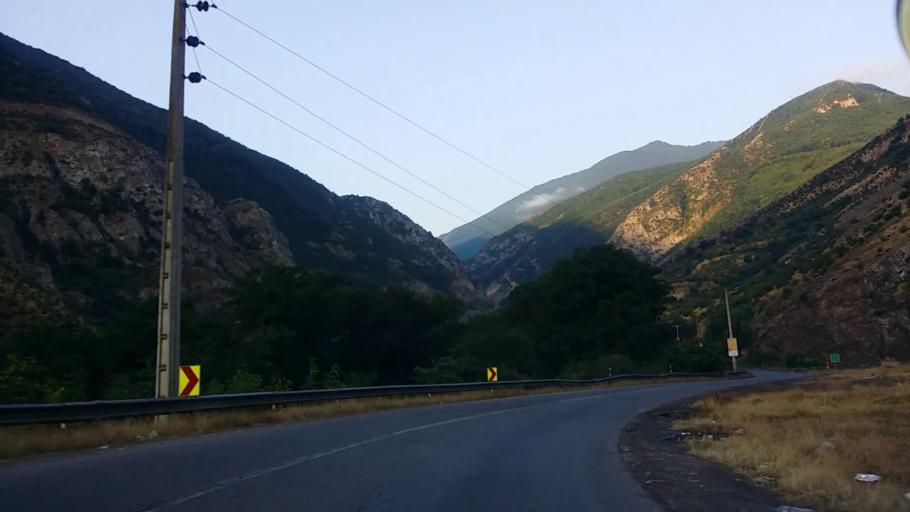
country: IR
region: Mazandaran
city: Chalus
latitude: 36.3788
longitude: 51.2742
